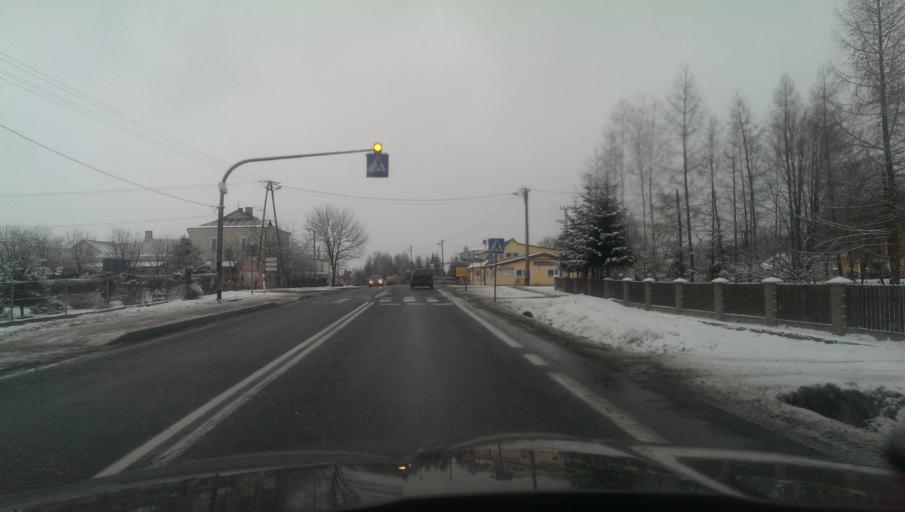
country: PL
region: Subcarpathian Voivodeship
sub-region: Powiat sanocki
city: Besko
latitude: 49.5863
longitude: 21.9563
